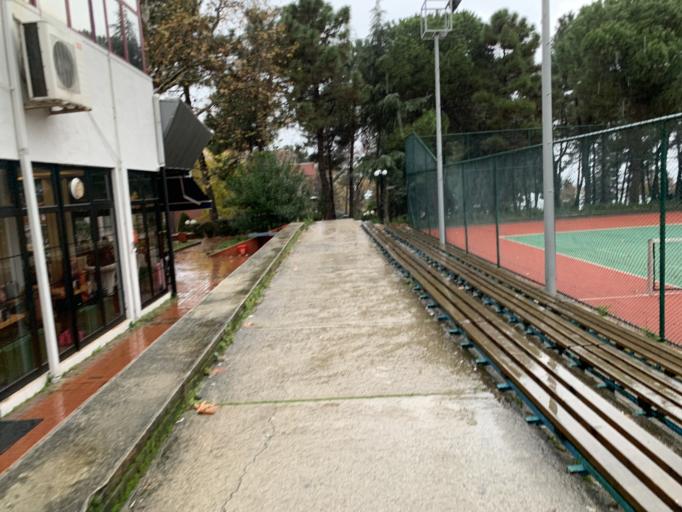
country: TR
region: Trabzon
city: Trabzon
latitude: 40.9965
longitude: 39.7683
